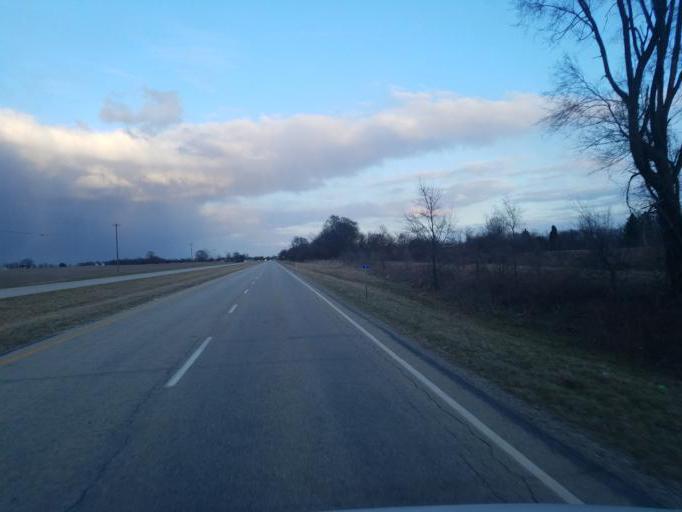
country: US
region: Indiana
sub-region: Henry County
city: Knightstown
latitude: 39.8021
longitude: -85.4613
